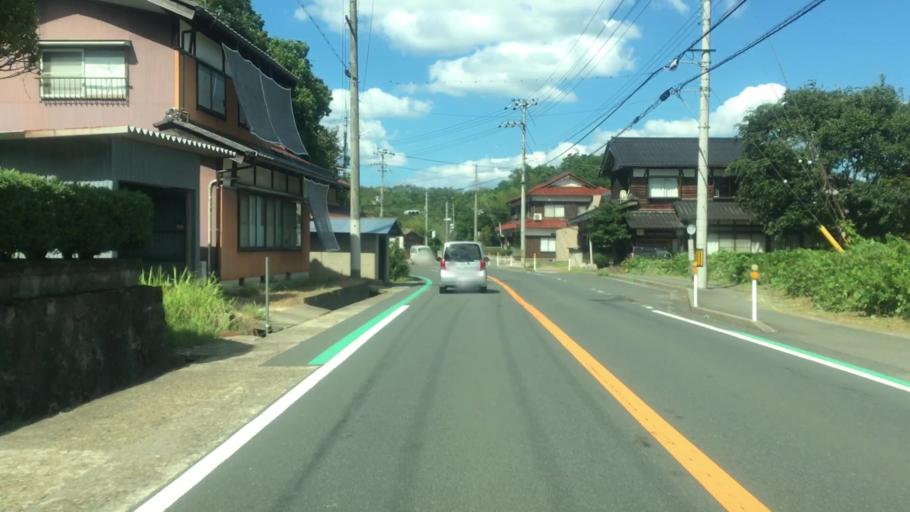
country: JP
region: Kyoto
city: Miyazu
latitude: 35.6120
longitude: 135.0540
